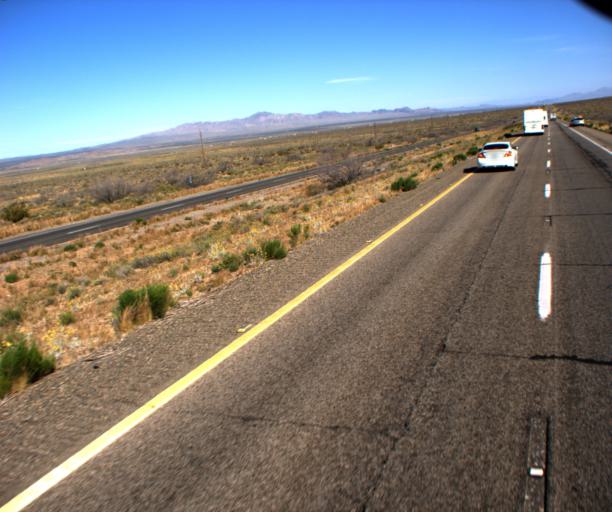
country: US
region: Arizona
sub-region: Mohave County
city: Dolan Springs
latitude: 35.4508
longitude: -114.2978
